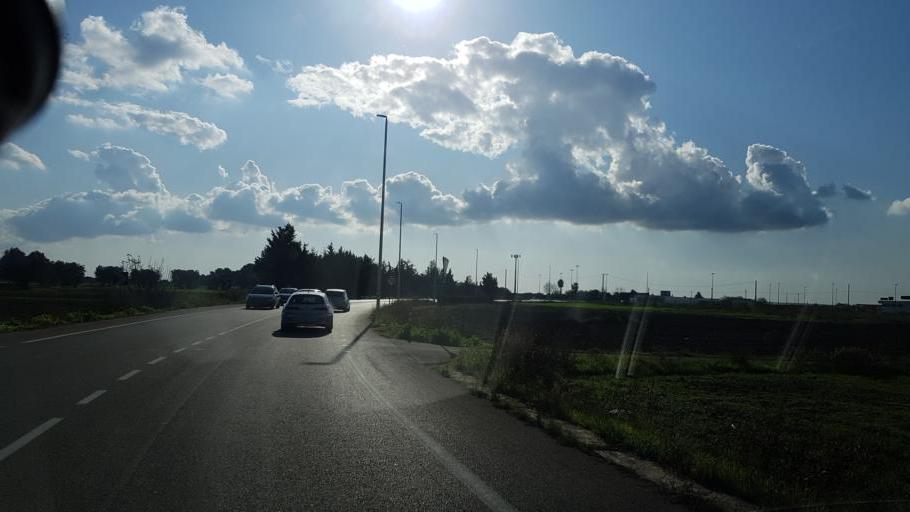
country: IT
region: Apulia
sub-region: Provincia di Lecce
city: Salice Salentino
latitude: 40.3766
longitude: 17.9693
